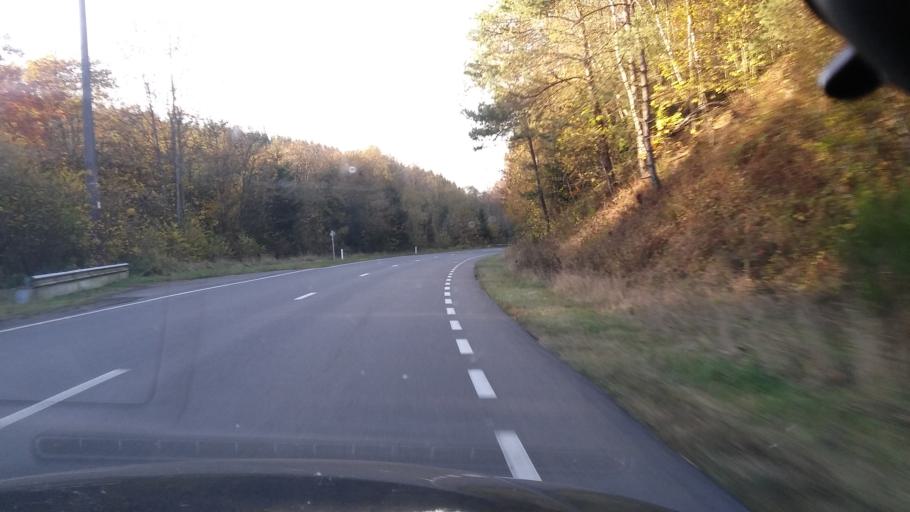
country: BE
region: Wallonia
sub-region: Province du Luxembourg
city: Bouillon
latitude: 49.7606
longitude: 5.0973
